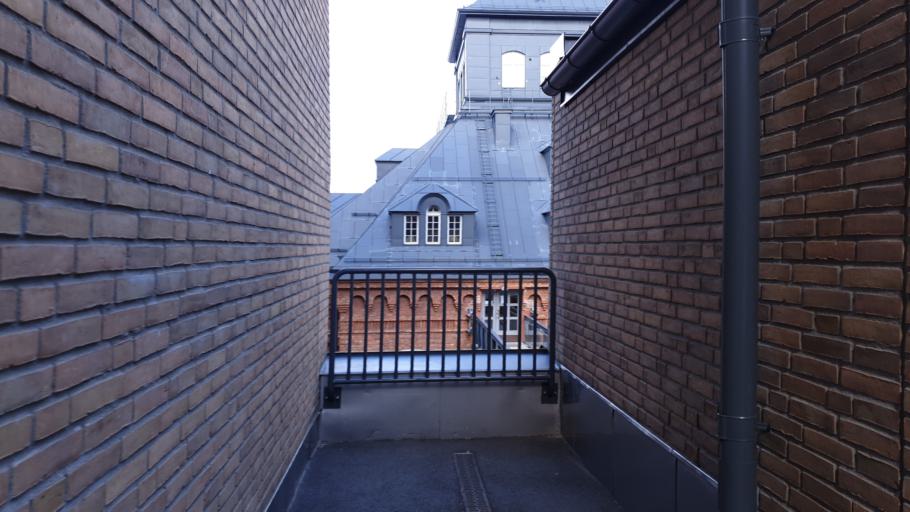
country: SE
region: Stockholm
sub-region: Nacka Kommun
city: Nacka
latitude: 59.3172
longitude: 18.1402
